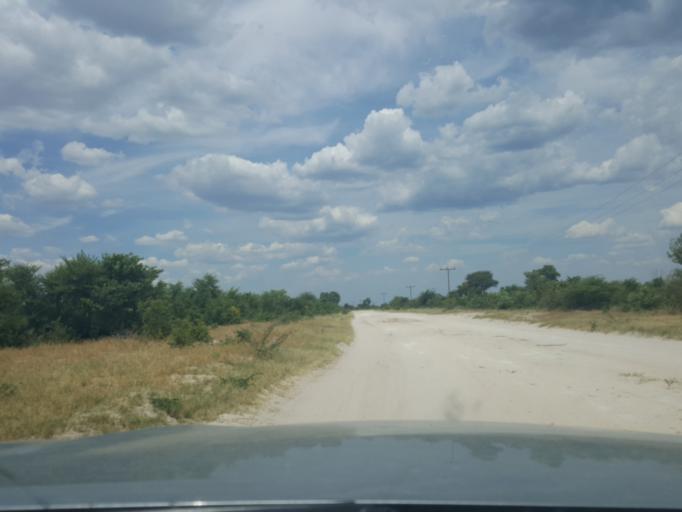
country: BW
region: North West
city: Shakawe
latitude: -18.5078
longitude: 22.1382
